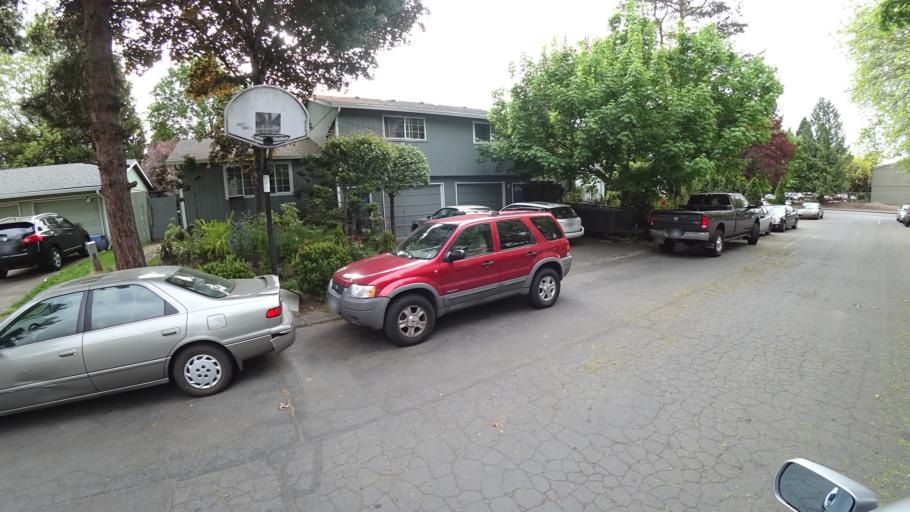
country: US
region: Oregon
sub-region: Washington County
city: Hillsboro
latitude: 45.5333
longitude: -122.9614
